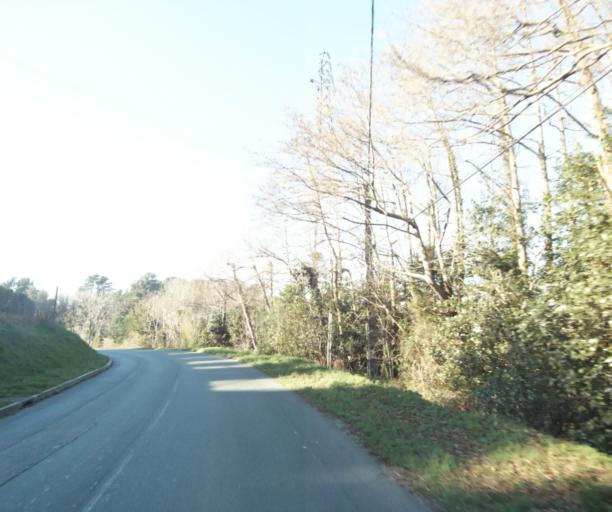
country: FR
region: Aquitaine
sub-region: Departement des Pyrenees-Atlantiques
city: Hendaye
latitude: 43.3557
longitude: -1.7421
